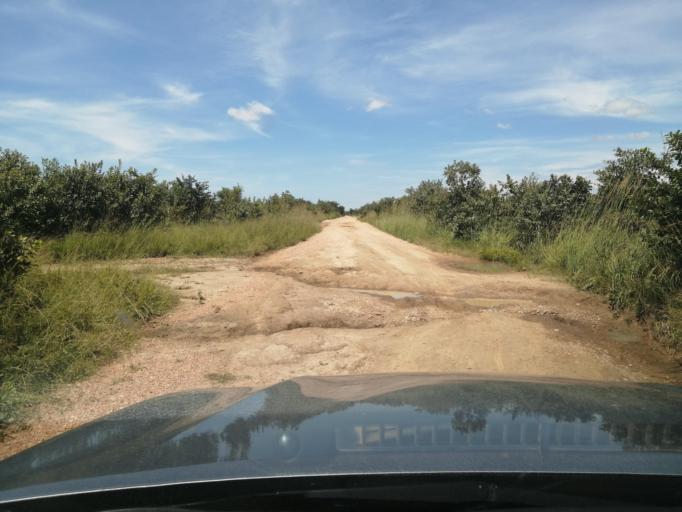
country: ZM
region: Central
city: Chibombo
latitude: -15.0358
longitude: 27.8259
